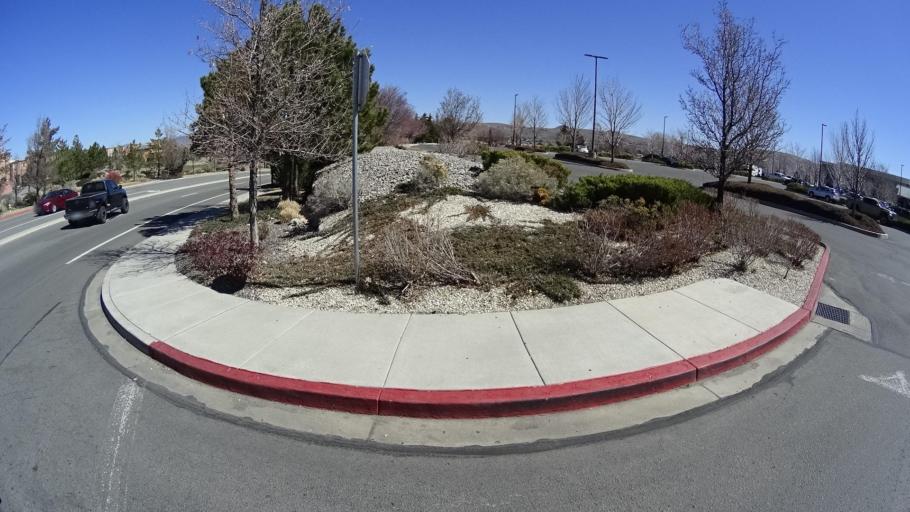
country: US
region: Nevada
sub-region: Washoe County
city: Sun Valley
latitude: 39.5803
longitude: -119.7398
